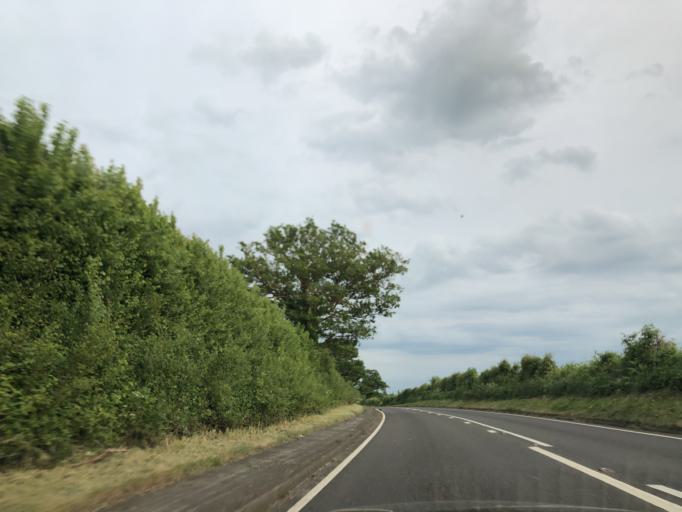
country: GB
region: England
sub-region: Warwickshire
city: Wroxall
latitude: 52.3135
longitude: -1.6661
